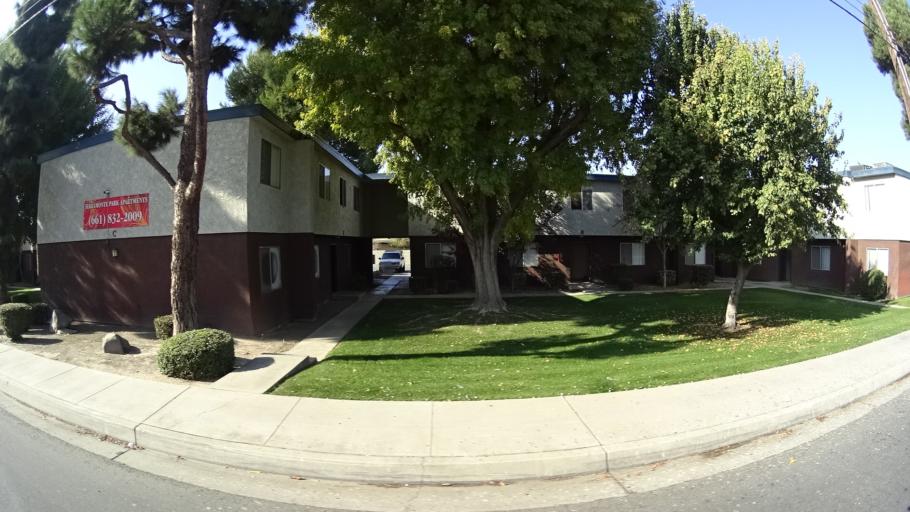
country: US
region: California
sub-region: Kern County
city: Bakersfield
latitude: 35.3231
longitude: -119.0214
